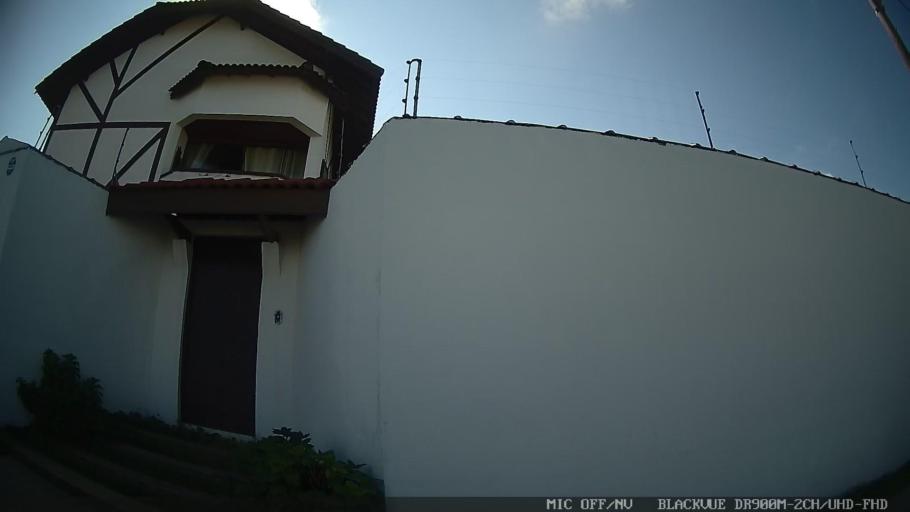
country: BR
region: Sao Paulo
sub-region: Peruibe
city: Peruibe
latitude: -24.2899
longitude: -46.9552
